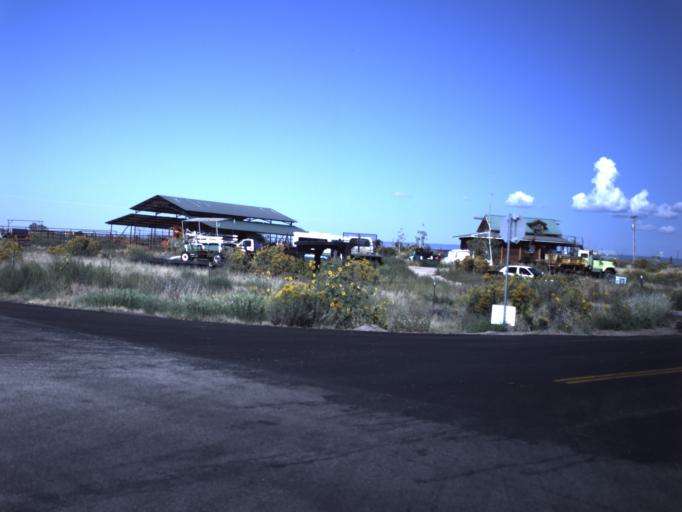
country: US
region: Utah
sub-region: San Juan County
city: Blanding
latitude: 37.5729
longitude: -109.4874
